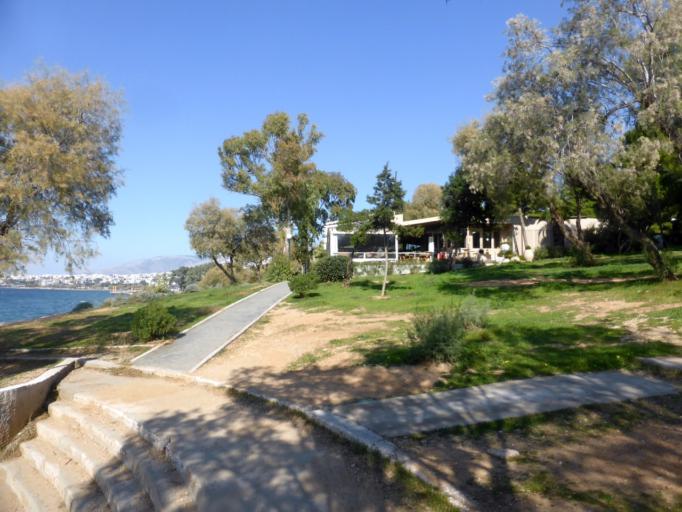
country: GR
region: Attica
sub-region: Nomarchia Anatolikis Attikis
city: Vouliagmeni
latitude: 37.8249
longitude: 23.7699
